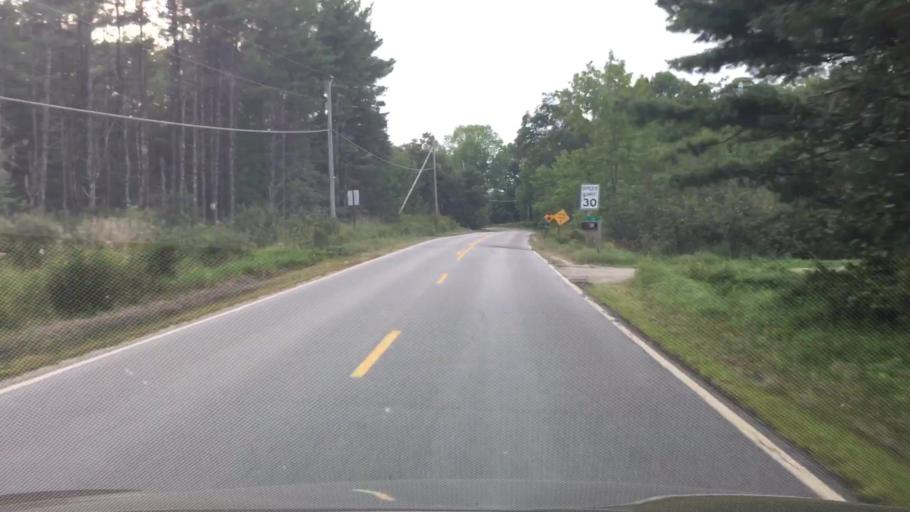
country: US
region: Maine
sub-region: Hancock County
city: Penobscot
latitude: 44.4513
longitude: -68.6984
